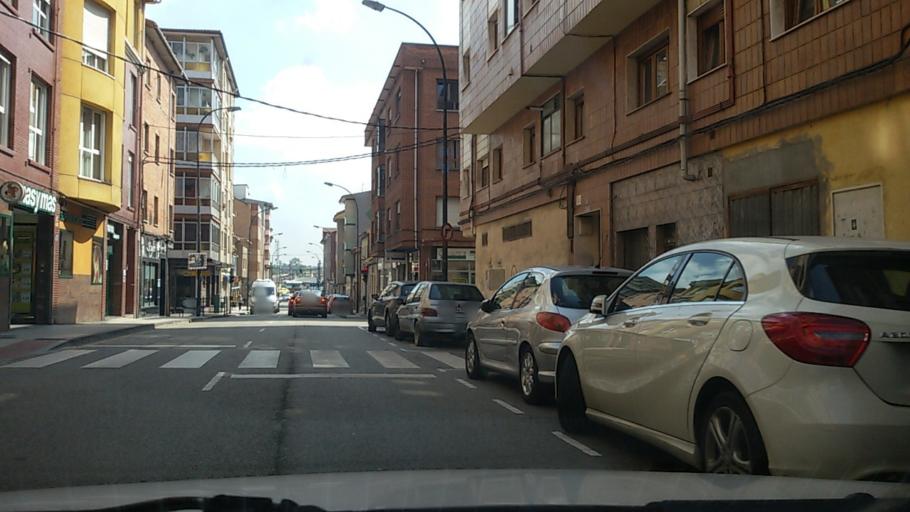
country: ES
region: Asturias
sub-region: Province of Asturias
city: Lugones
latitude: 43.4423
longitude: -5.8184
